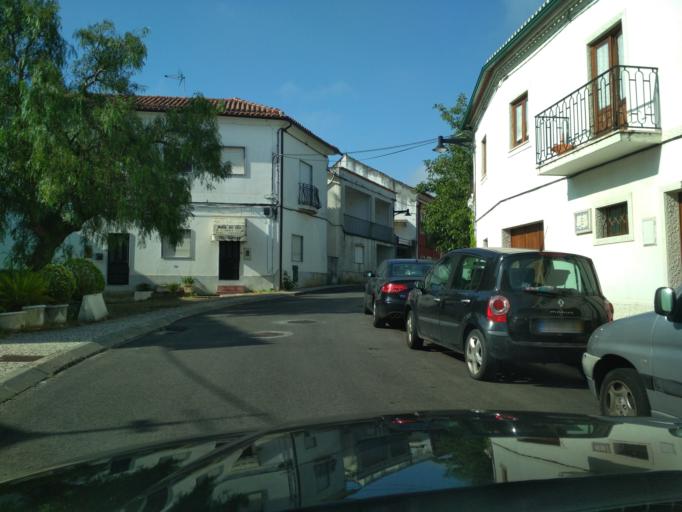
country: PT
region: Coimbra
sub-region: Condeixa-A-Nova
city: Condeixa-a-Nova
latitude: 40.1373
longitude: -8.4699
